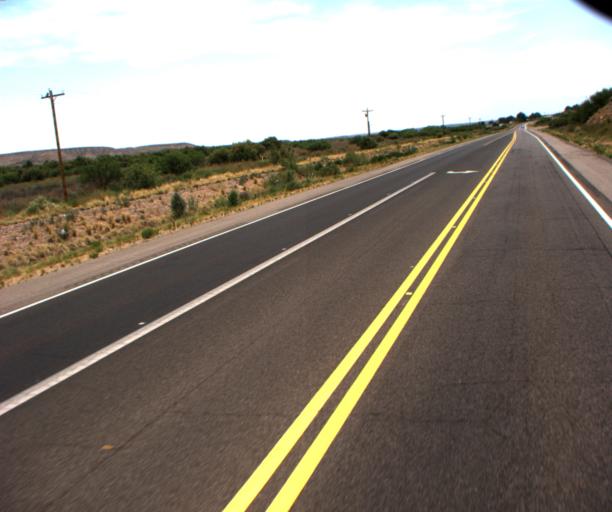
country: US
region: Arizona
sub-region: Graham County
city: Bylas
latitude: 33.1551
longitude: -110.1295
